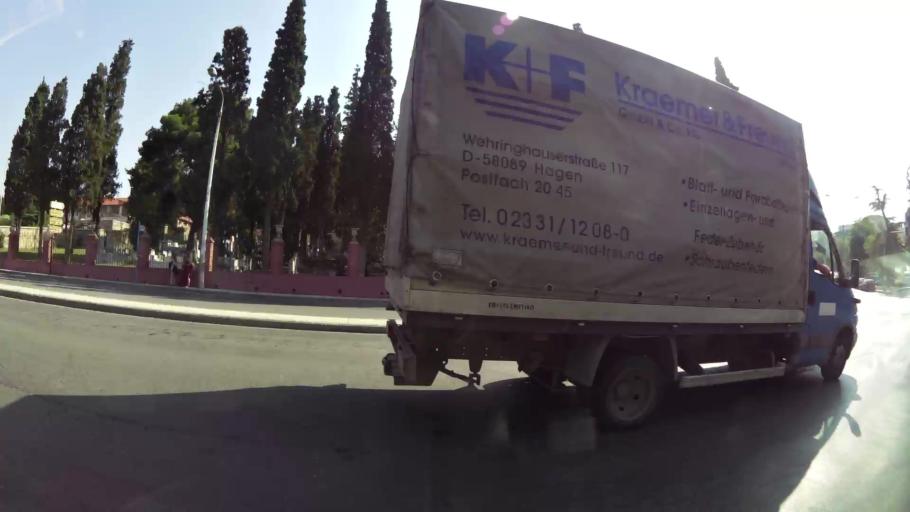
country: GR
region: Central Macedonia
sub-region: Nomos Thessalonikis
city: Agios Pavlos
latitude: 40.6345
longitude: 22.9561
